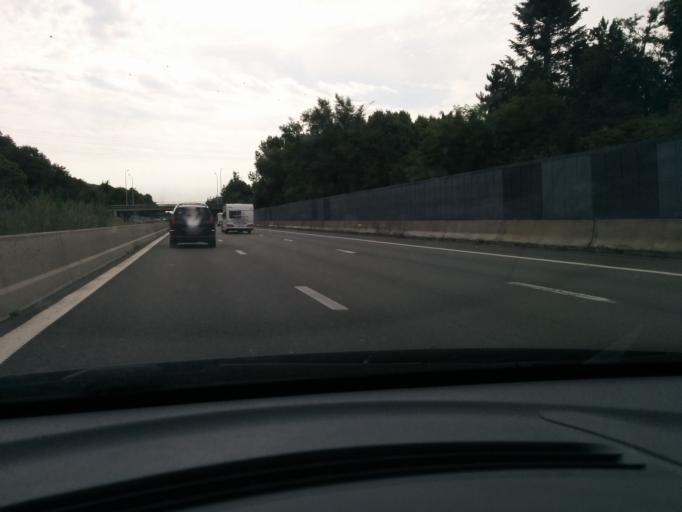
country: BE
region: Flanders
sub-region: Provincie West-Vlaanderen
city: Zedelgem
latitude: 51.1785
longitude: 3.1296
